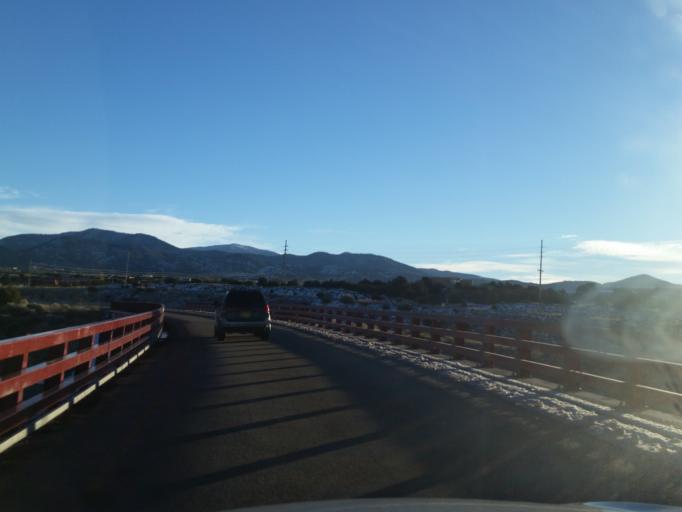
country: US
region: New Mexico
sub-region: Santa Fe County
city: Santa Fe
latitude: 35.6321
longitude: -105.9567
